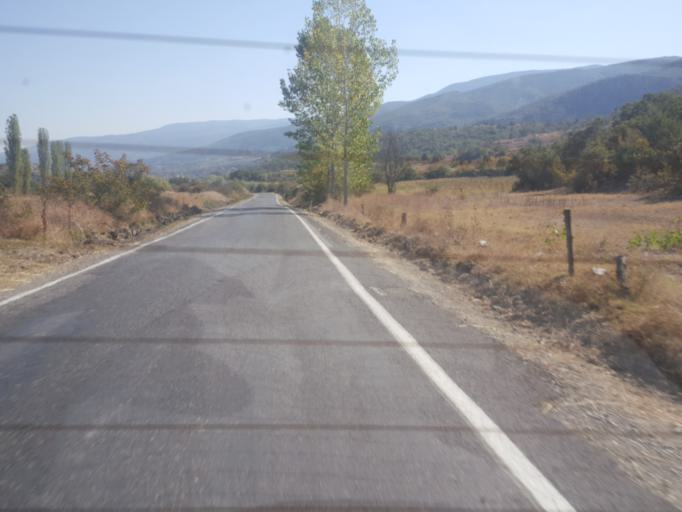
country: TR
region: Kastamonu
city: Tosya
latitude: 40.9862
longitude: 34.0867
